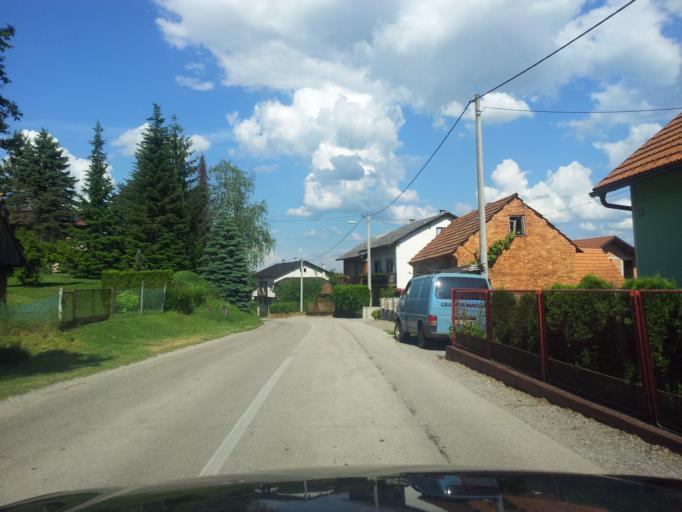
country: HR
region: Karlovacka
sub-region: Grad Karlovac
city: Karlovac
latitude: 45.4209
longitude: 15.4749
